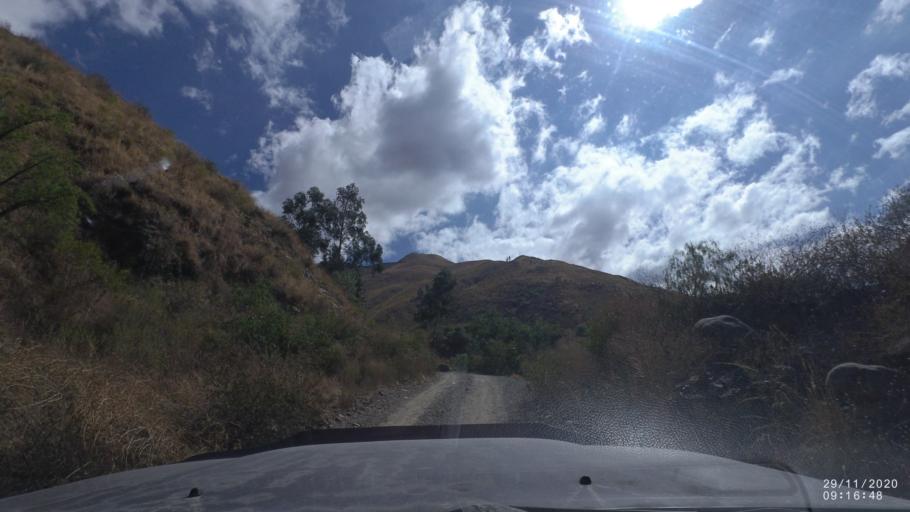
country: BO
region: Cochabamba
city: Cochabamba
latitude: -17.3259
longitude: -66.1853
